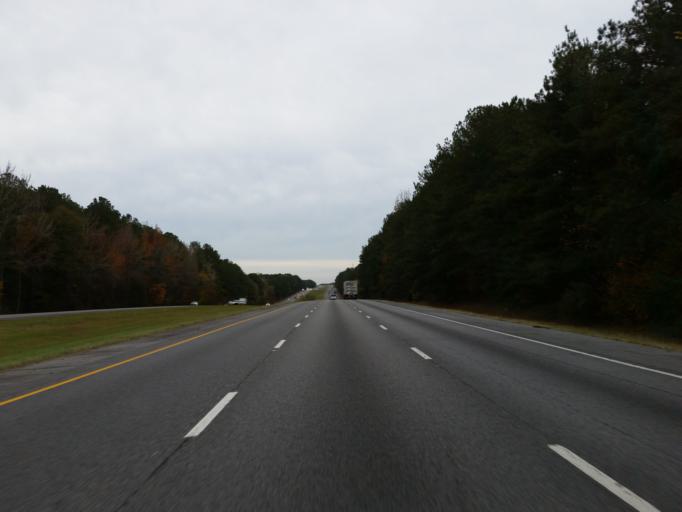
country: US
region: Georgia
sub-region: Houston County
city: Perry
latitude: 32.3707
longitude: -83.7685
